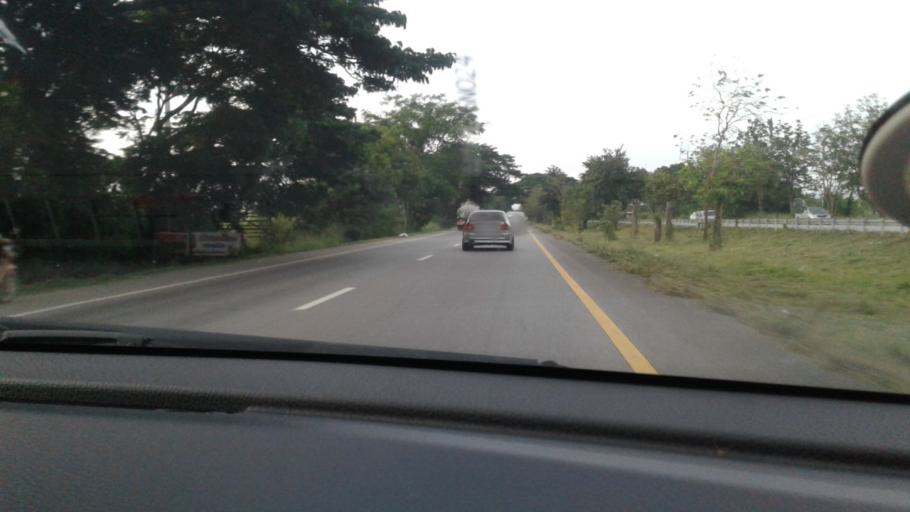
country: TH
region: Prachuap Khiri Khan
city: Hua Hin
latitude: 12.6062
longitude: 99.8615
